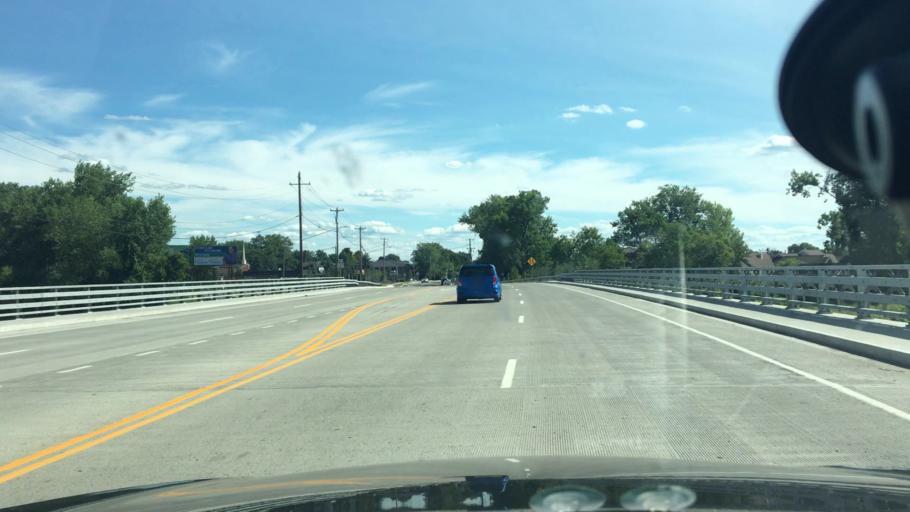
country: US
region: New York
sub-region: Erie County
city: Sloan
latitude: 42.8705
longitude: -78.7875
